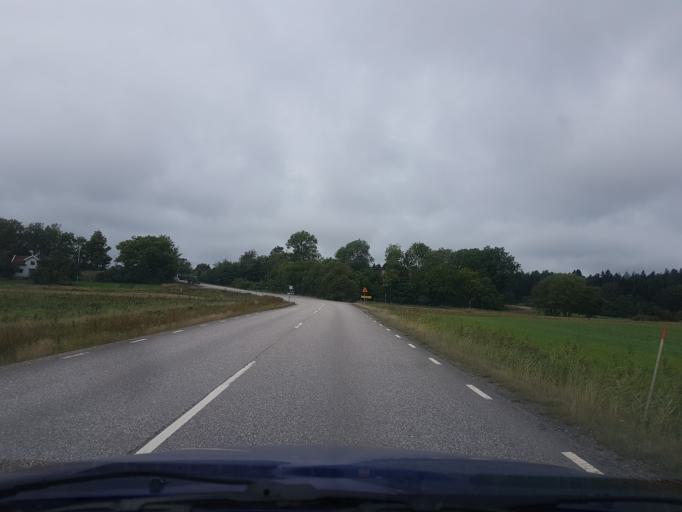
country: SE
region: Vaestra Goetaland
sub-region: Ale Kommun
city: Skepplanda
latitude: 57.9457
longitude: 12.1749
